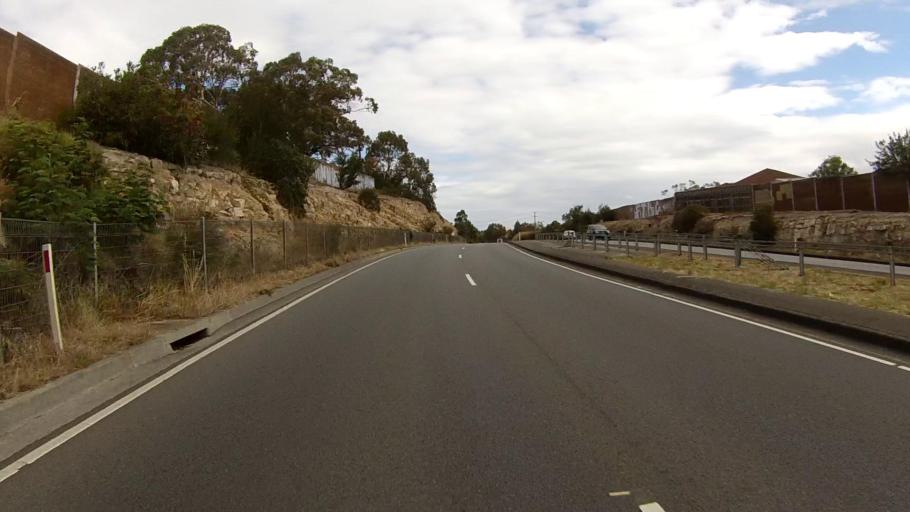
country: AU
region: Tasmania
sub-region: Clarence
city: Howrah
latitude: -42.8820
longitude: 147.4104
